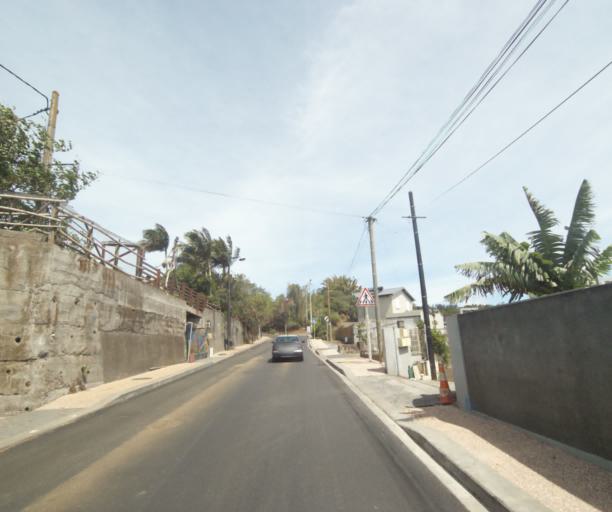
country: RE
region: Reunion
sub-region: Reunion
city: Saint-Paul
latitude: -21.0407
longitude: 55.3011
